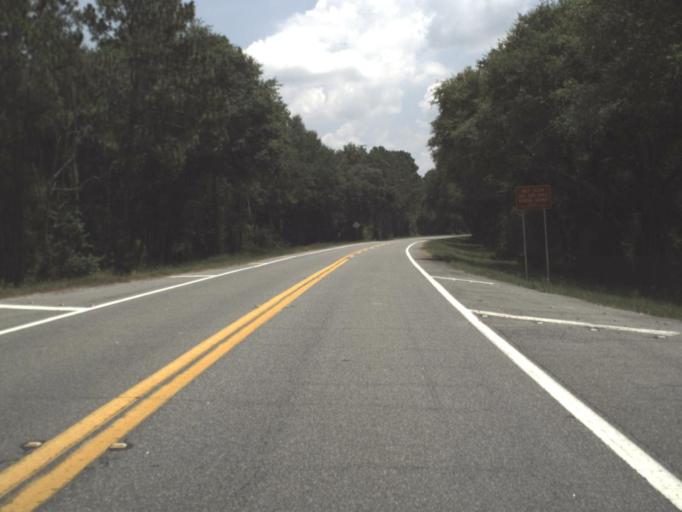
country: US
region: Florida
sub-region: Madison County
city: Madison
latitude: 30.4859
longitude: -83.2344
